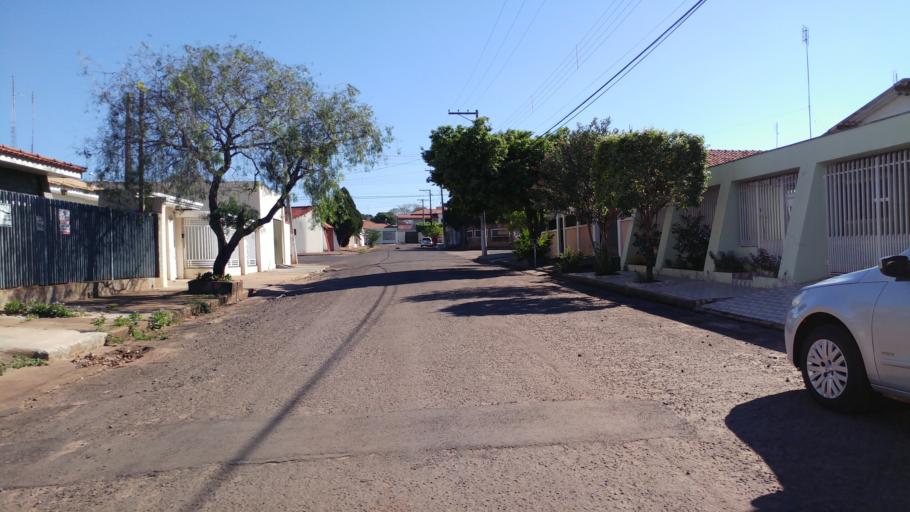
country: BR
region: Sao Paulo
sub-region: Paraguacu Paulista
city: Paraguacu Paulista
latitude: -22.4054
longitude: -50.5770
